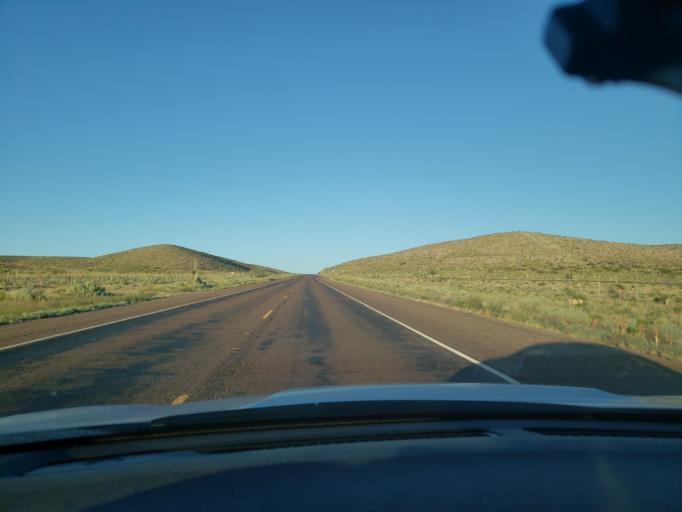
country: US
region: Texas
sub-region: El Paso County
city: Homestead Meadows South
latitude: 31.8269
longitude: -105.8987
